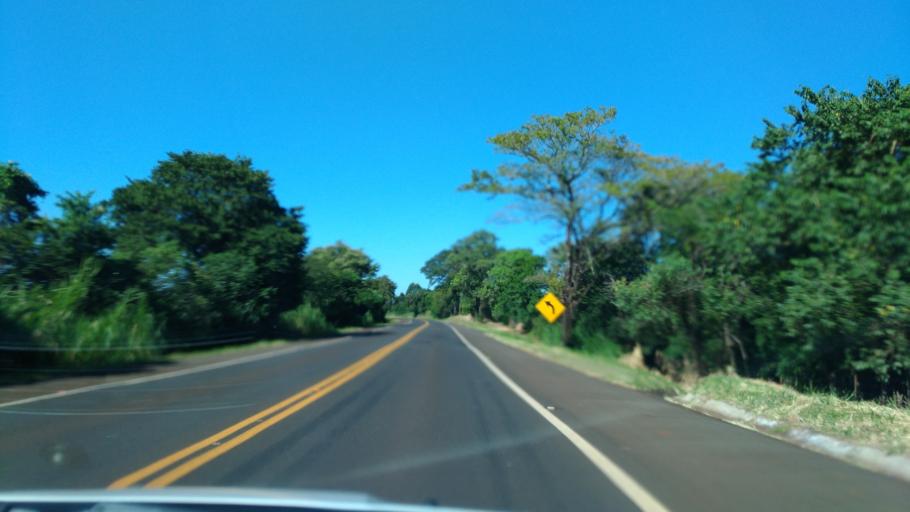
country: BR
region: Parana
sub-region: Assai
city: Assai
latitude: -23.2740
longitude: -50.8242
